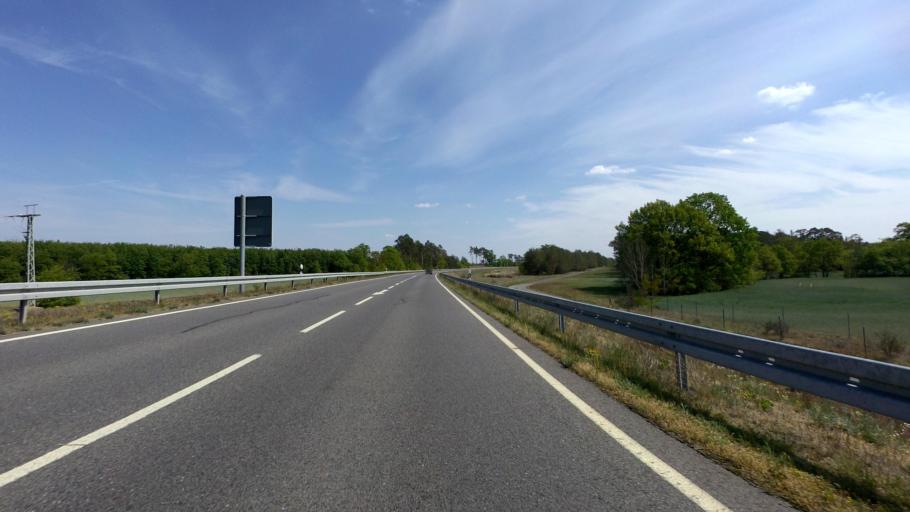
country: DE
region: Brandenburg
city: Cottbus
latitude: 51.7836
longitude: 14.3816
